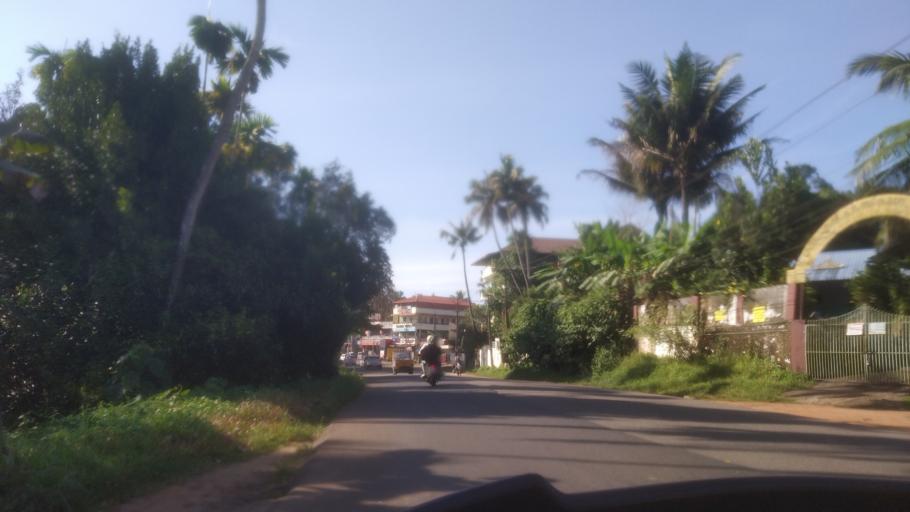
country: IN
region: Kerala
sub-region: Ernakulam
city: Ramamangalam
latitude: 9.9802
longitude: 76.5213
